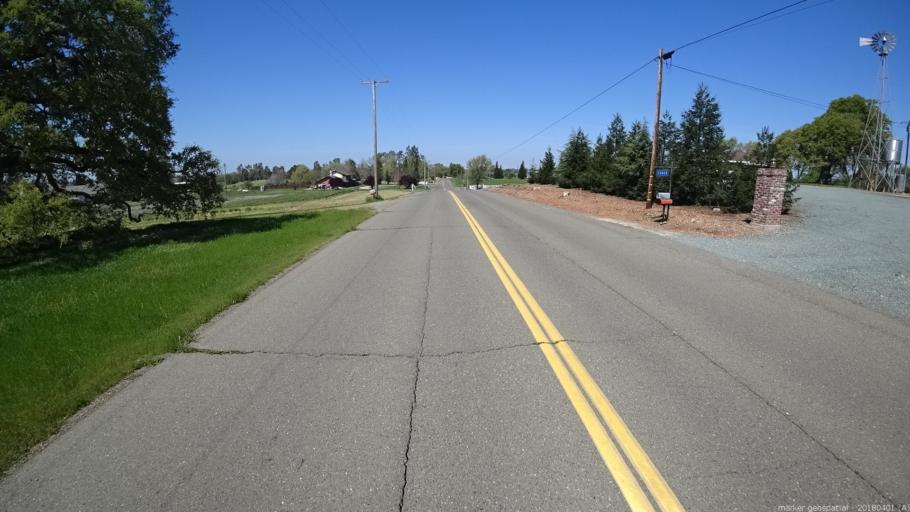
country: US
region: California
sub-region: Sacramento County
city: Wilton
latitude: 38.4192
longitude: -121.2150
